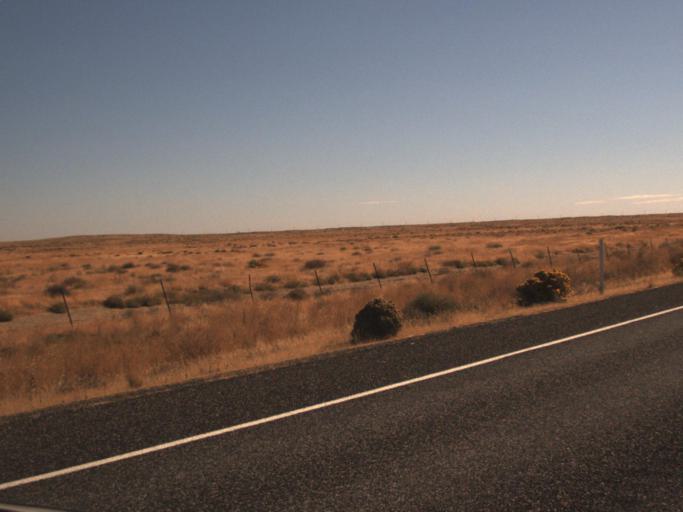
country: US
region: Washington
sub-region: Benton County
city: Benton City
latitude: 46.4816
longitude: -119.5724
